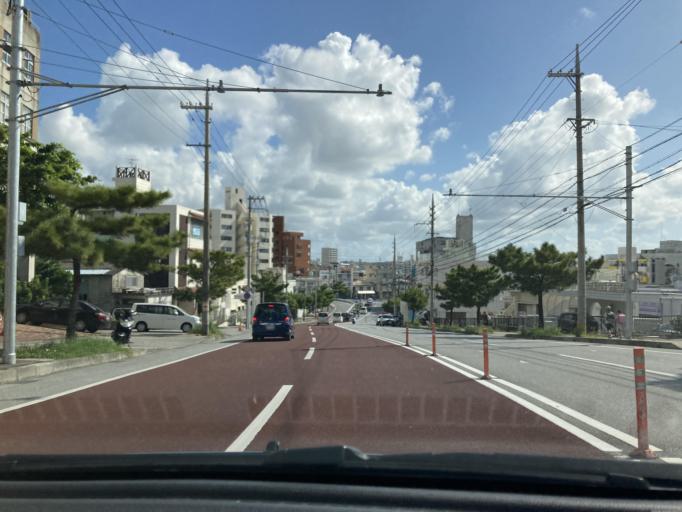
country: JP
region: Okinawa
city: Naha-shi
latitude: 26.2198
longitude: 127.7026
